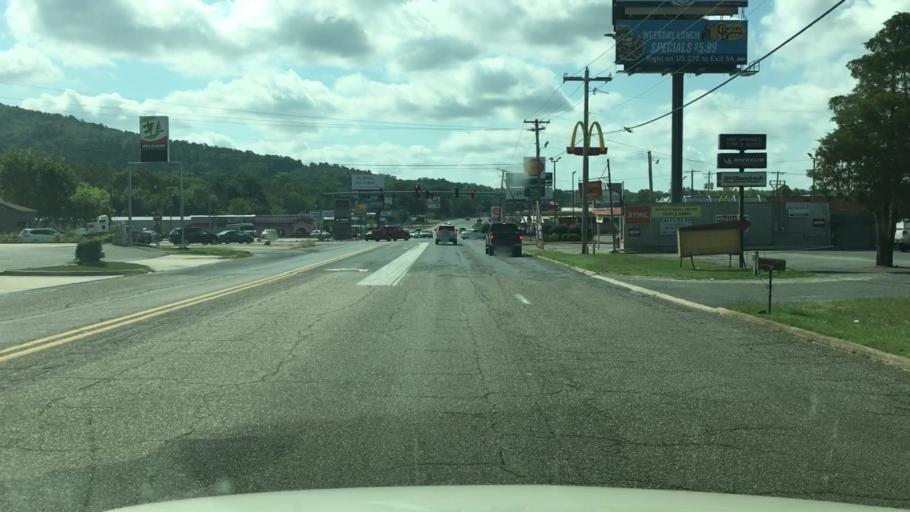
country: US
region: Arkansas
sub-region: Garland County
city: Piney
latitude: 34.5040
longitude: -93.1269
